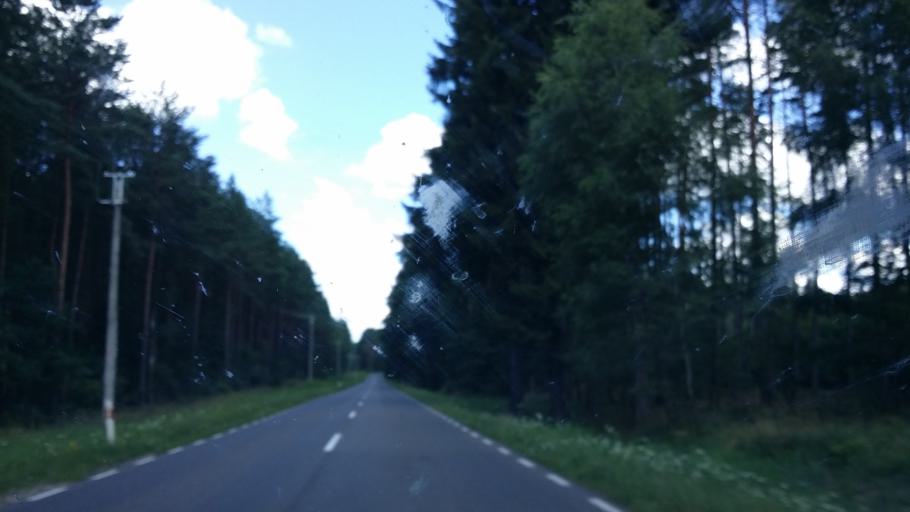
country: PL
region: West Pomeranian Voivodeship
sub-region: Powiat swidwinski
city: Slawoborze
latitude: 53.8687
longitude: 15.7294
